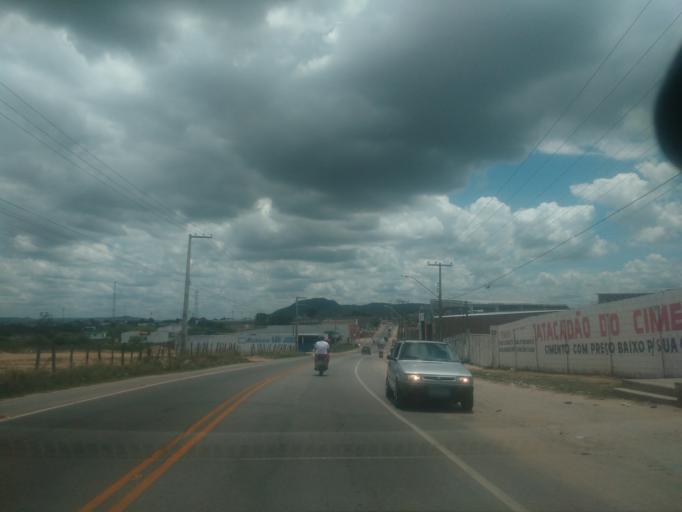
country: BR
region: Alagoas
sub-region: Uniao Dos Palmares
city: Uniao dos Palmares
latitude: -9.1529
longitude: -36.0169
